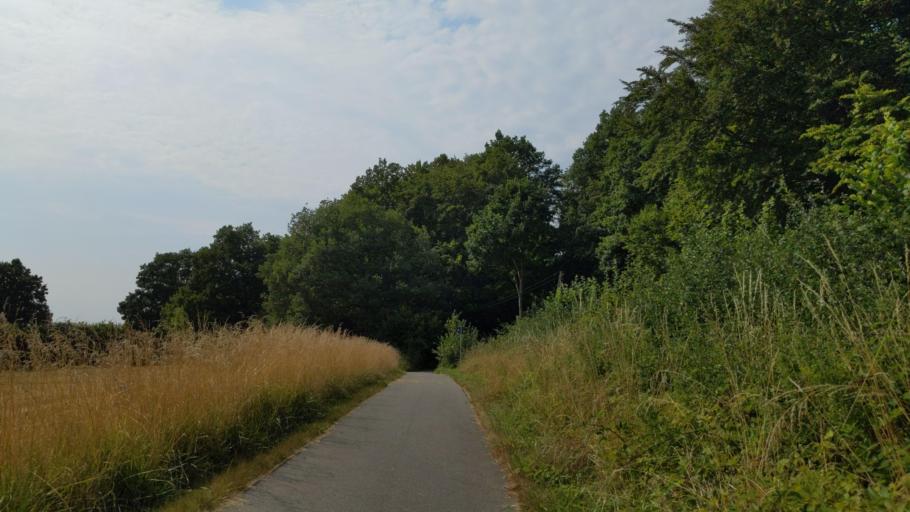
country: DE
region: Schleswig-Holstein
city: Behlendorf
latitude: 53.7046
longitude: 10.6546
